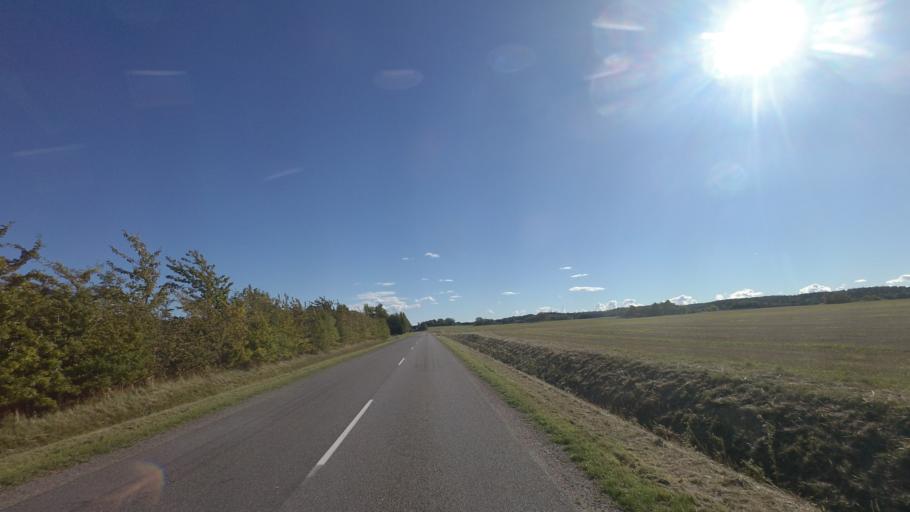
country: DK
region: Capital Region
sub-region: Bornholm Kommune
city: Nexo
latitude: 55.1108
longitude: 15.1106
